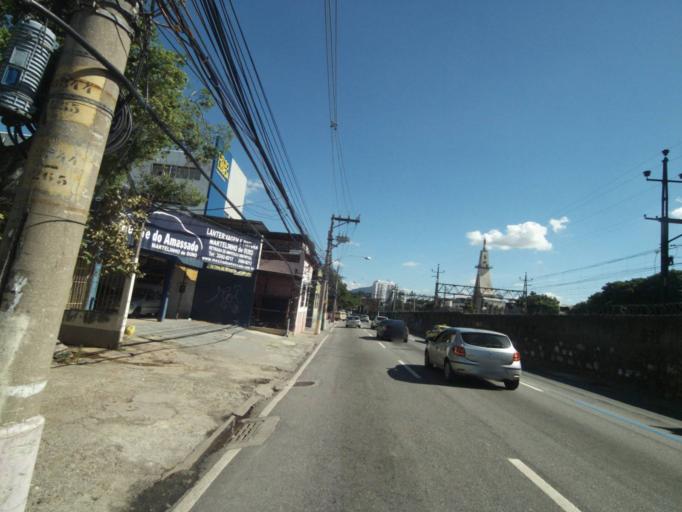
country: BR
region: Rio de Janeiro
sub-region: Rio De Janeiro
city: Rio de Janeiro
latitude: -22.9023
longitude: -43.2643
